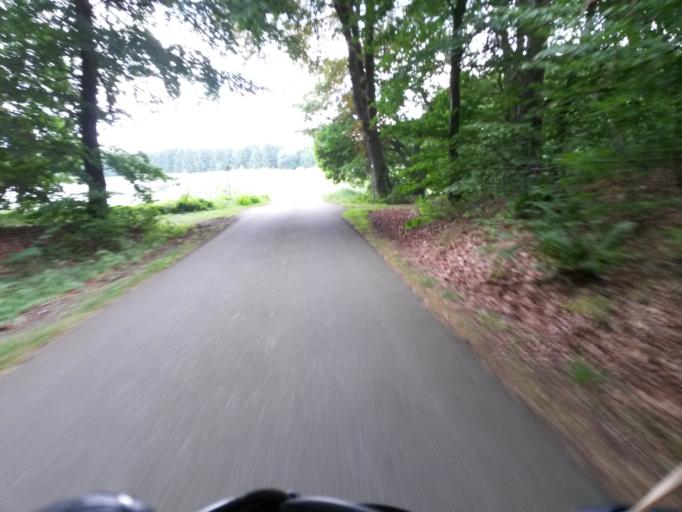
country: DE
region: Brandenburg
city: Angermunde
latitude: 53.0471
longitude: 13.9424
